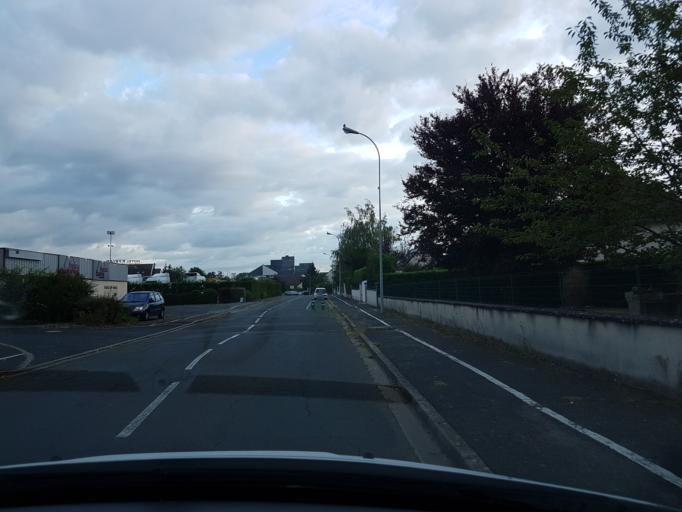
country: FR
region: Centre
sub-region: Departement d'Indre-et-Loire
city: Chambray-les-Tours
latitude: 47.3362
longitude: 0.7076
